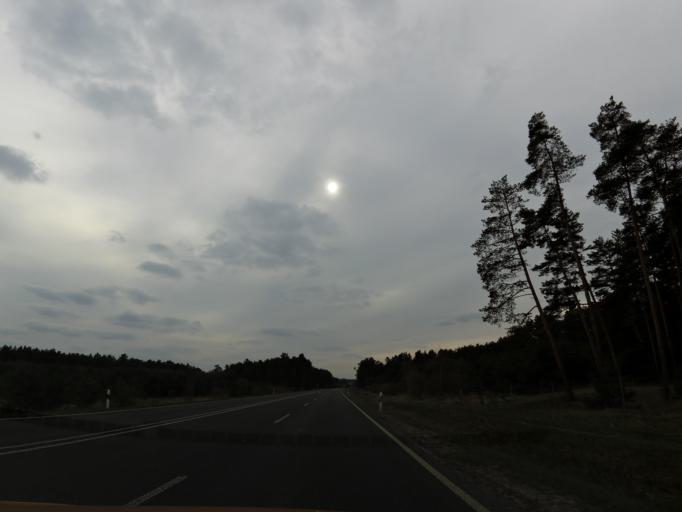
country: DE
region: Brandenburg
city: Mullrose
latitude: 52.2665
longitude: 14.4290
